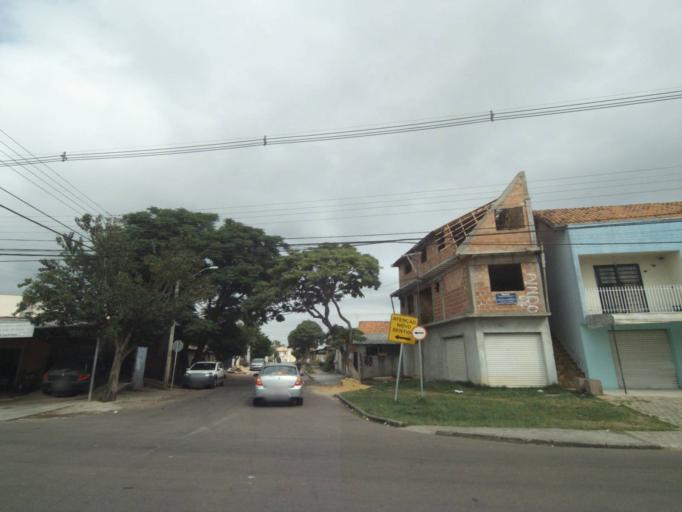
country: BR
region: Parana
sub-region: Sao Jose Dos Pinhais
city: Sao Jose dos Pinhais
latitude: -25.5386
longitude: -49.2548
